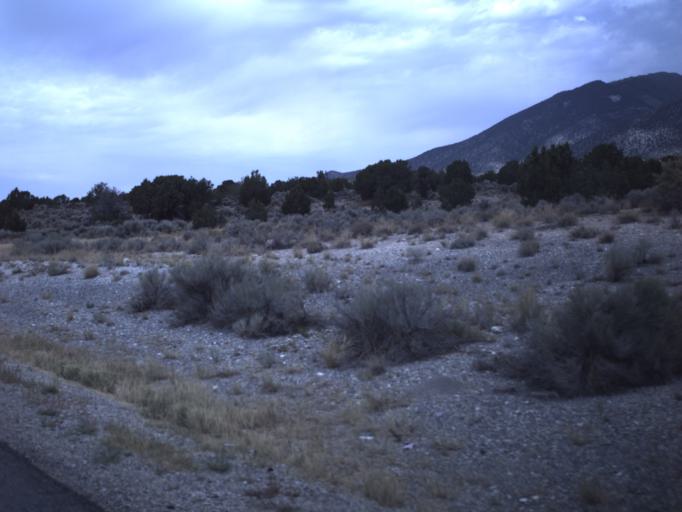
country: US
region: Utah
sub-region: Tooele County
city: Tooele
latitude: 40.3322
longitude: -112.2960
